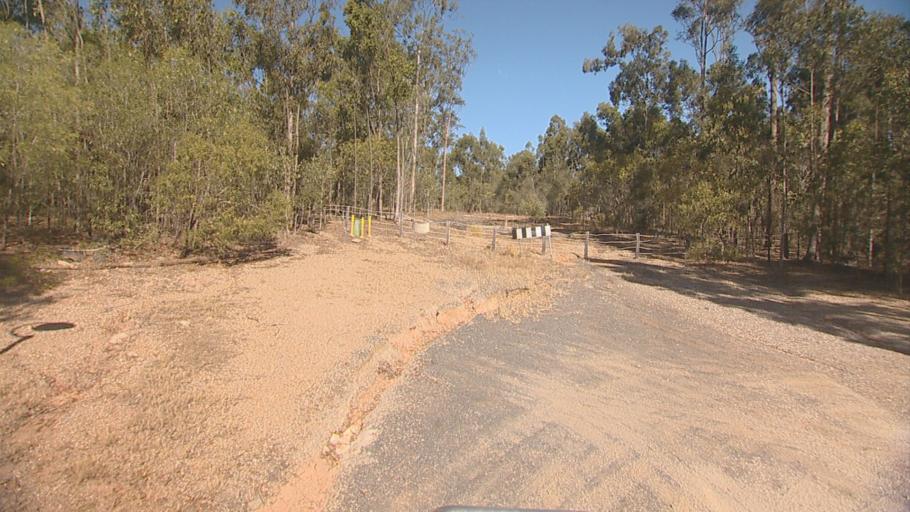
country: AU
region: Queensland
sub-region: Logan
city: North Maclean
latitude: -27.7553
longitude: 152.9403
